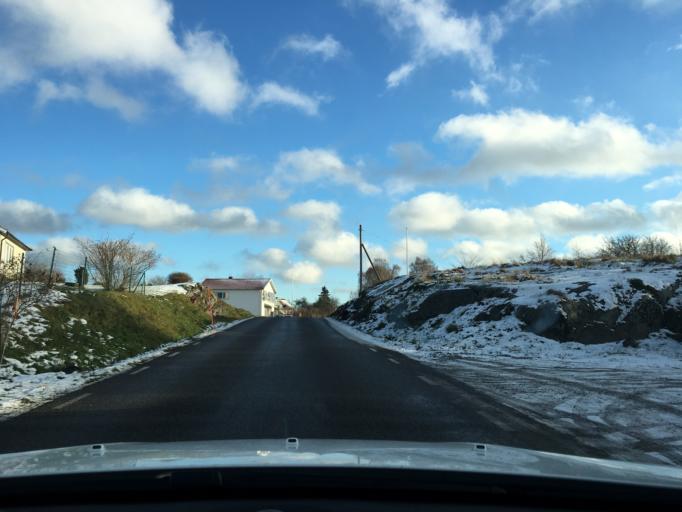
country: SE
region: Vaestra Goetaland
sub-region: Tjorns Kommun
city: Myggenas
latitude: 58.0514
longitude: 11.7090
